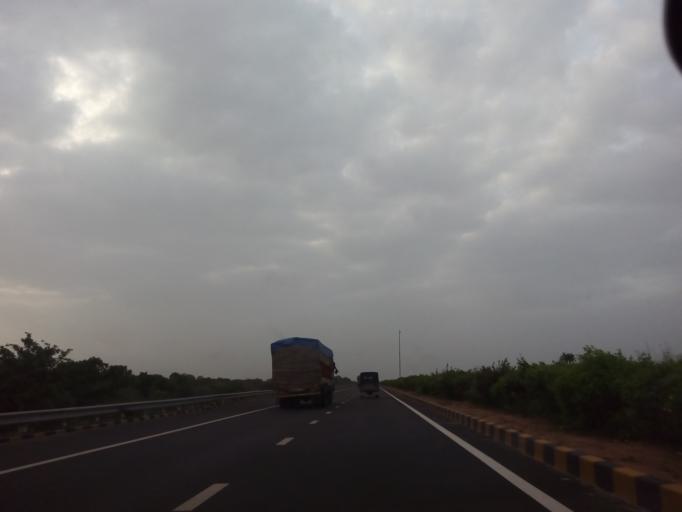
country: IN
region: Gujarat
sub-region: Kheda
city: Mahemdavad
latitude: 22.9335
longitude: 72.7269
